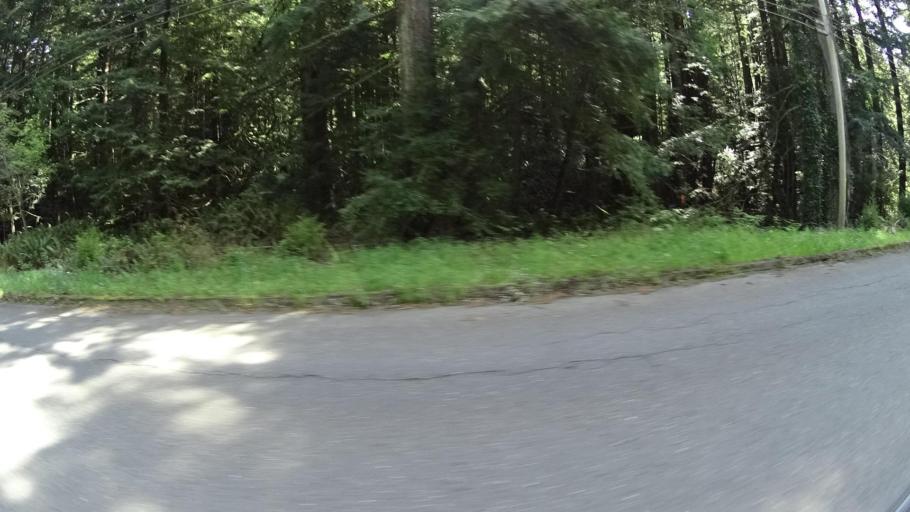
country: US
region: California
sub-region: Humboldt County
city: Hydesville
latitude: 40.5687
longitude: -124.1180
